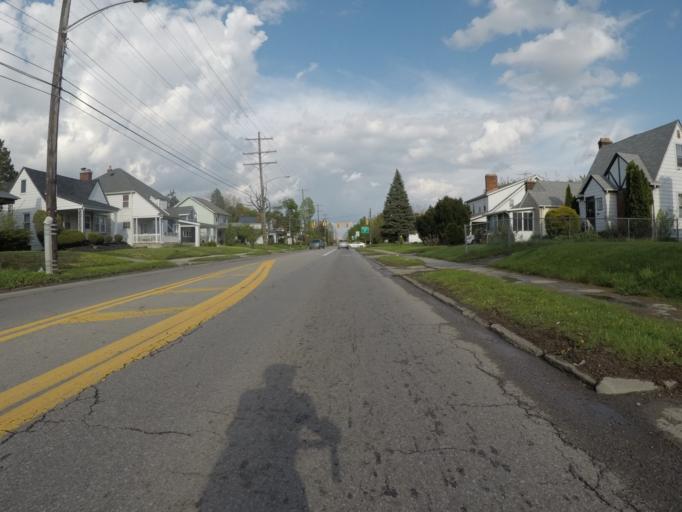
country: US
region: Ohio
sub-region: Franklin County
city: Bexley
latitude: 40.0139
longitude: -82.9734
